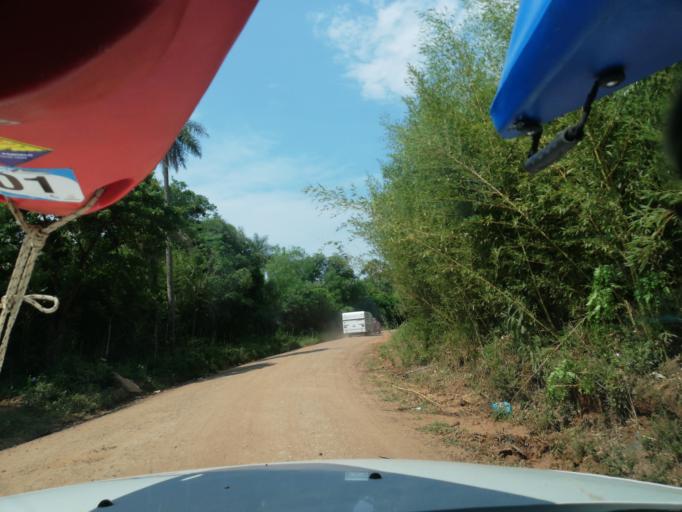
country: AR
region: Misiones
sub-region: Departamento de San Ignacio
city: San Ignacio
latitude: -27.2649
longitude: -55.5529
